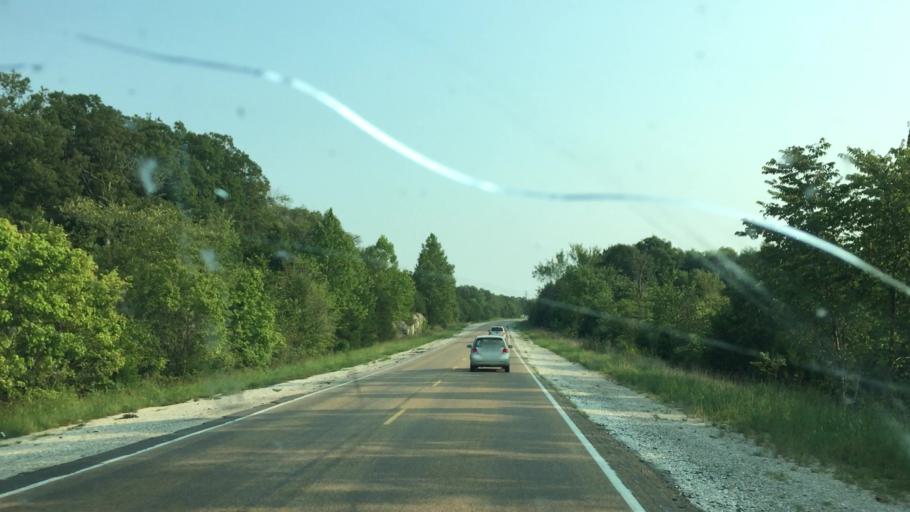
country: US
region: Missouri
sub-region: Pulaski County
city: Richland
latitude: 37.7788
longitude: -92.4093
